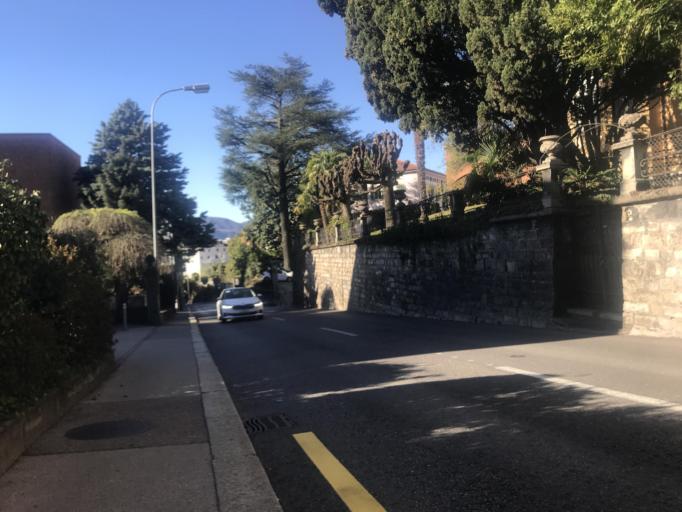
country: CH
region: Ticino
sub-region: Lugano District
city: Massagno
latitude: 46.0117
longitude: 8.9468
